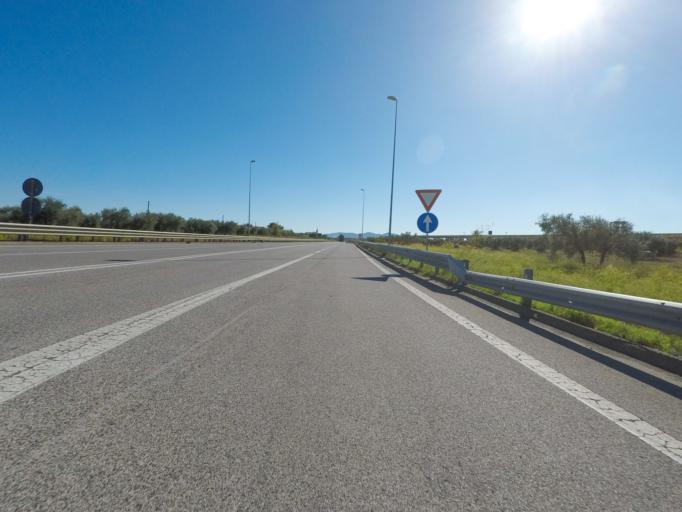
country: IT
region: Tuscany
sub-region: Provincia di Grosseto
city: Grosseto
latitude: 42.7713
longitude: 11.1459
